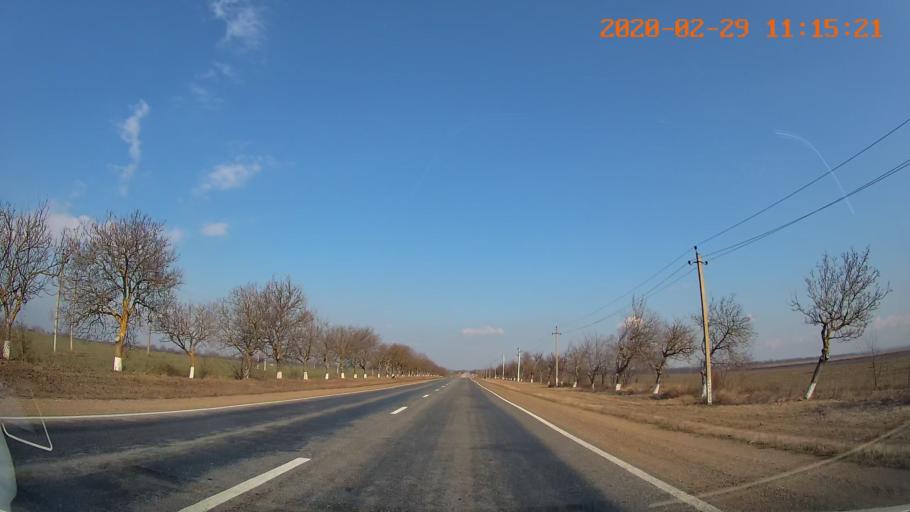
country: MD
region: Telenesti
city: Dubasari
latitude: 47.2932
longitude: 29.1649
